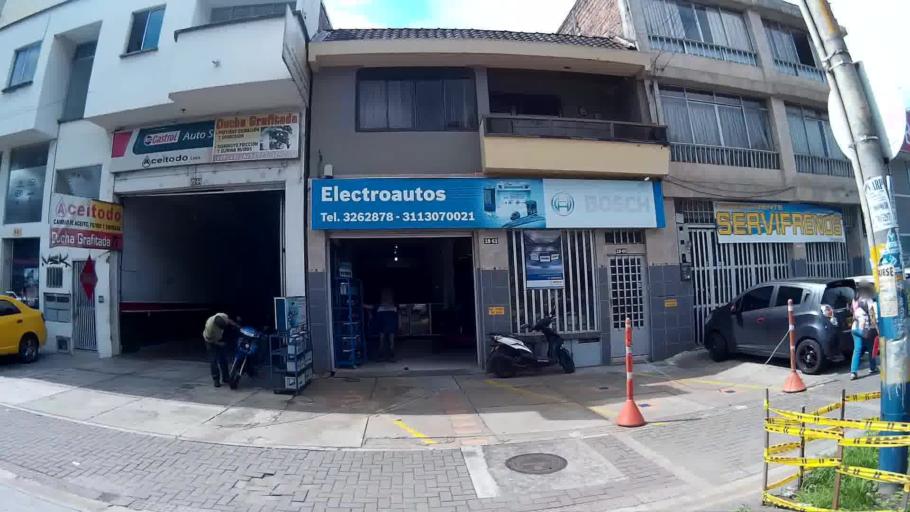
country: CO
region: Risaralda
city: Pereira
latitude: 4.8108
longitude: -75.7030
